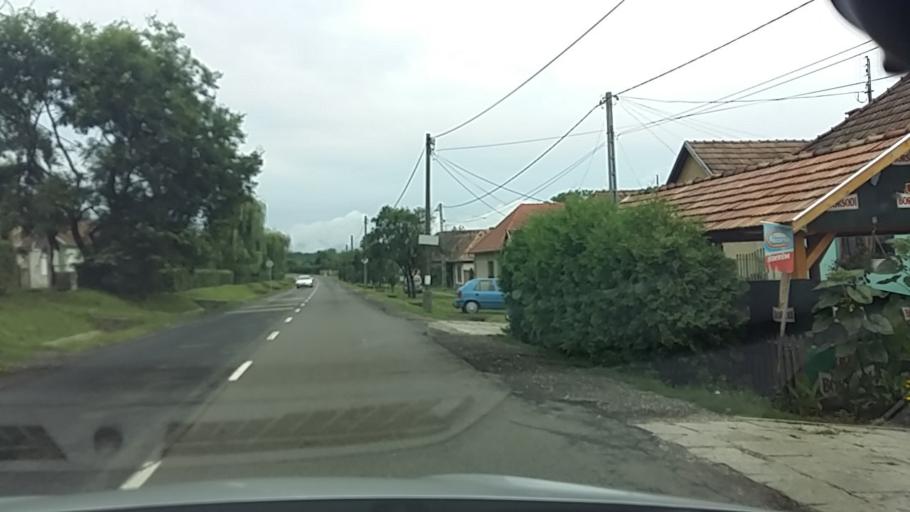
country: HU
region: Pest
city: Szob
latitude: 47.8404
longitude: 18.8297
